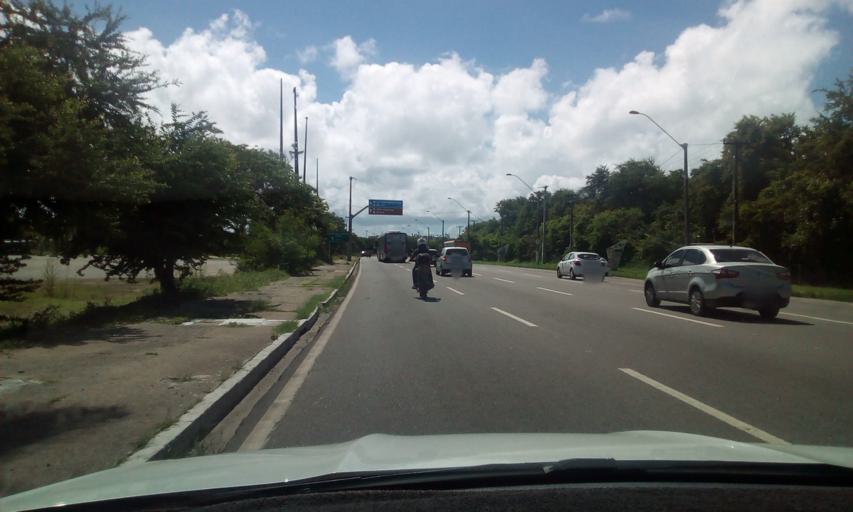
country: BR
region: Pernambuco
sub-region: Olinda
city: Olinda
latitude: -8.0319
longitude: -34.8659
